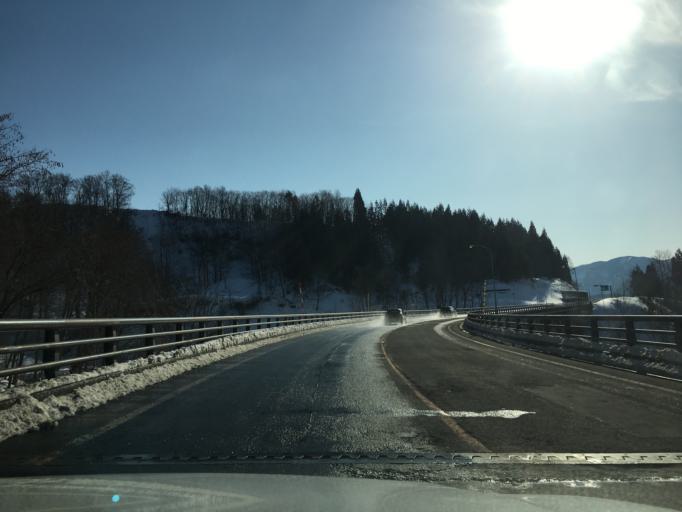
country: JP
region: Yamagata
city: Tsuruoka
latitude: 38.5761
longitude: 139.9431
